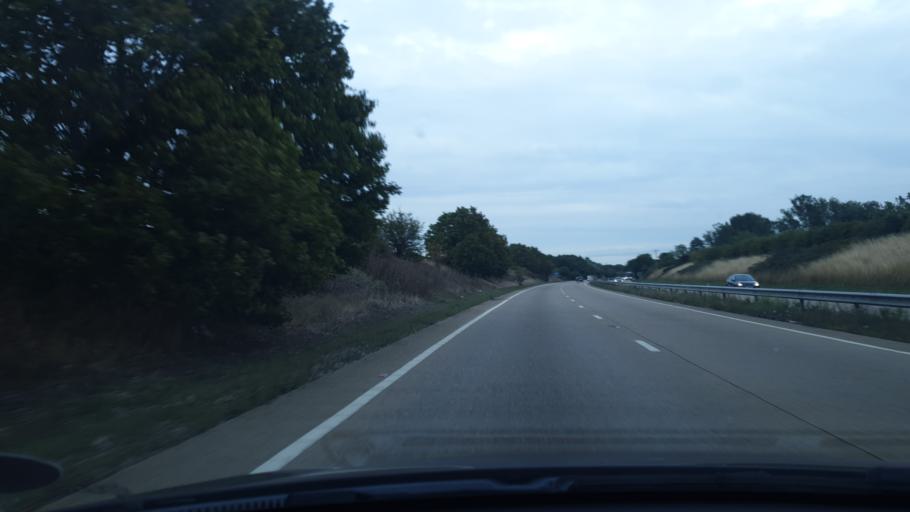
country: GB
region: England
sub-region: Essex
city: Alresford
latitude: 51.8967
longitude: 1.0004
